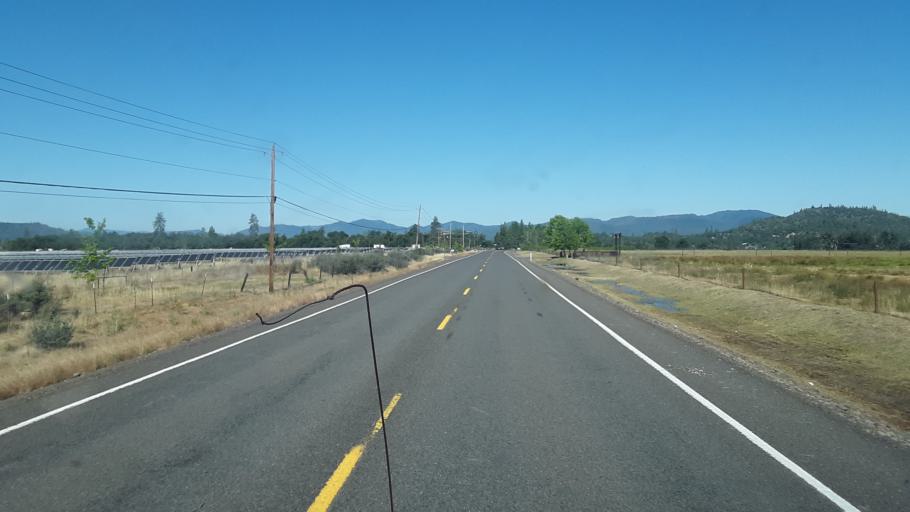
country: US
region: Oregon
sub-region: Jackson County
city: Eagle Point
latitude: 42.5237
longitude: -122.8285
